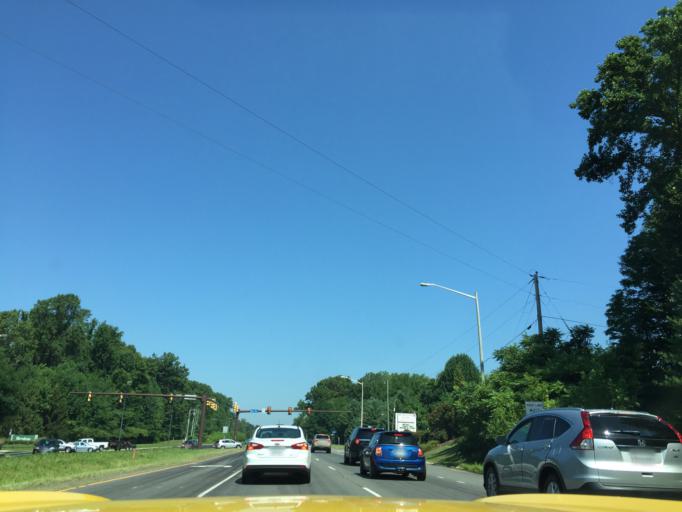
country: US
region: Virginia
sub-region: Fairfax County
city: Dranesville
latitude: 38.9941
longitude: -77.3354
